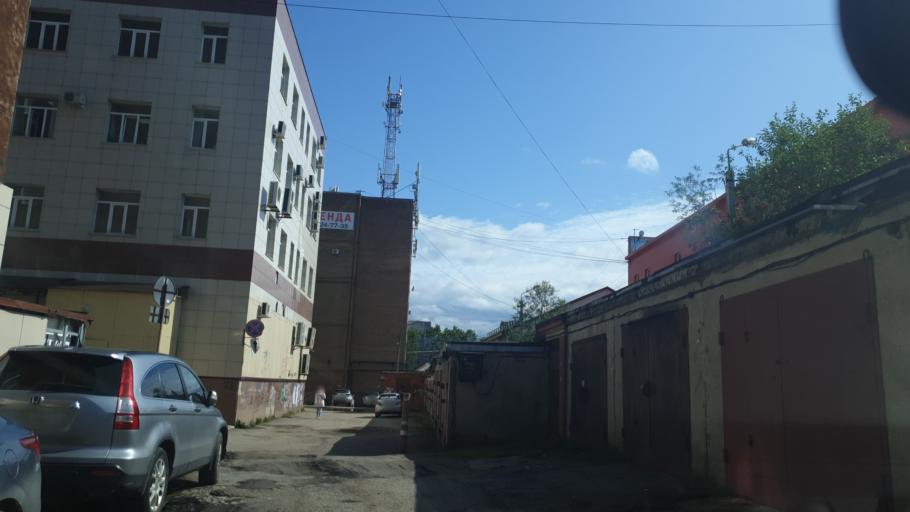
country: RU
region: Komi Republic
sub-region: Syktyvdinskiy Rayon
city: Syktyvkar
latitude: 61.6636
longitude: 50.8324
